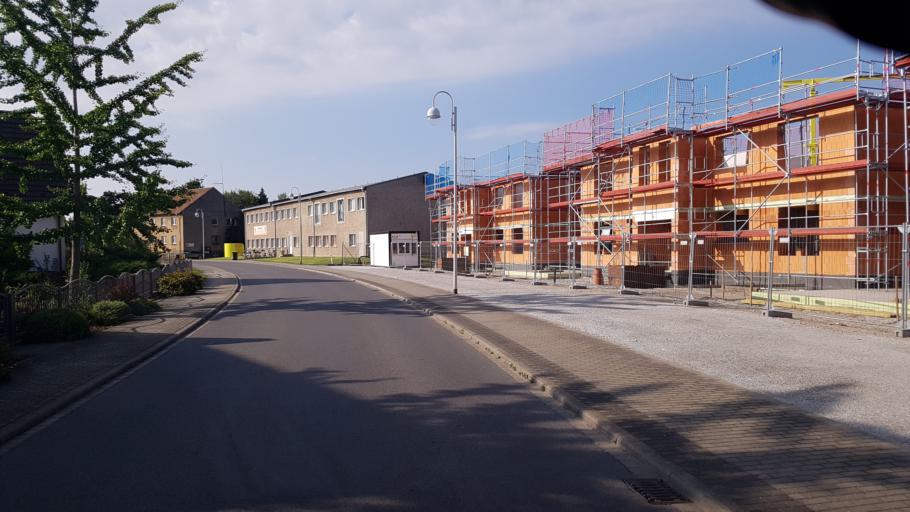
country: DE
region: Brandenburg
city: Luckau
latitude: 51.8559
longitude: 13.7212
